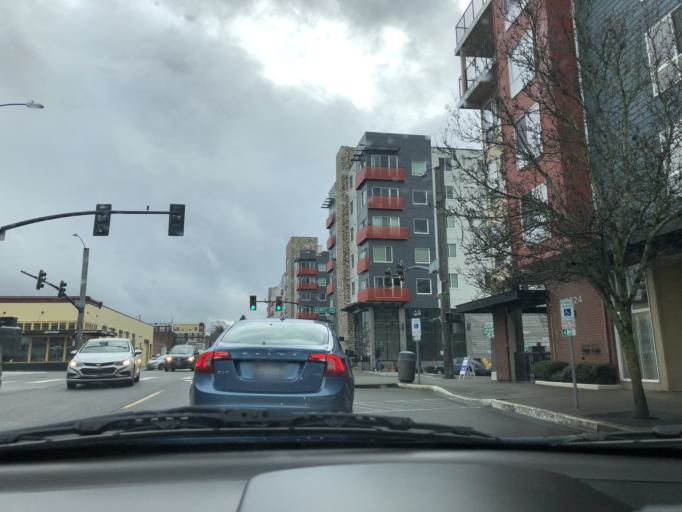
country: US
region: Washington
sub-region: Snohomish County
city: Everett
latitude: 47.9797
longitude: -122.2129
